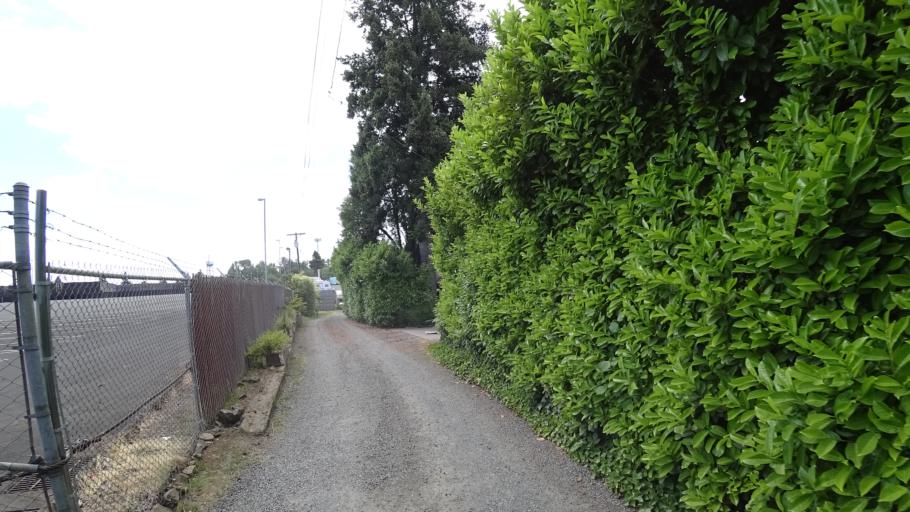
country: US
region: Oregon
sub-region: Washington County
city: West Haven
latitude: 45.6024
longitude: -122.7687
